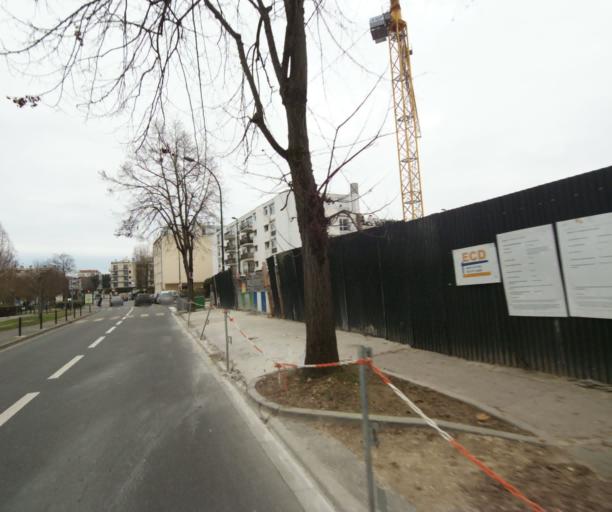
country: FR
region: Ile-de-France
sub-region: Departement des Hauts-de-Seine
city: Saint-Cloud
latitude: 48.8524
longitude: 2.2033
